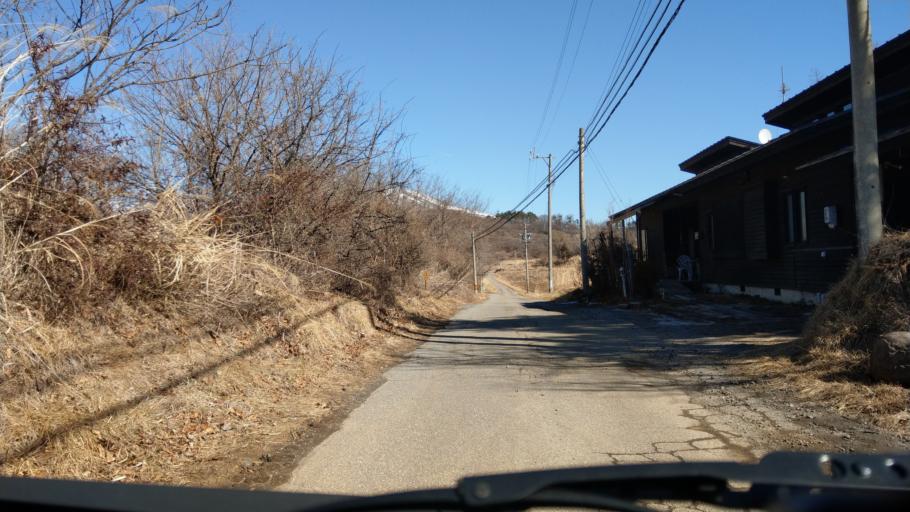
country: JP
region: Nagano
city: Komoro
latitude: 36.3106
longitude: 138.3970
